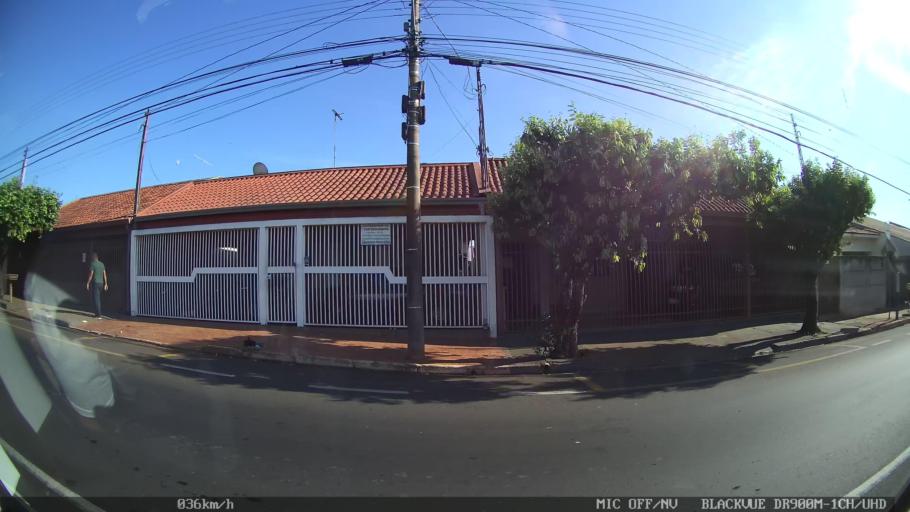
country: BR
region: Sao Paulo
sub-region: Sao Jose Do Rio Preto
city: Sao Jose do Rio Preto
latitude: -20.7783
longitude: -49.4021
